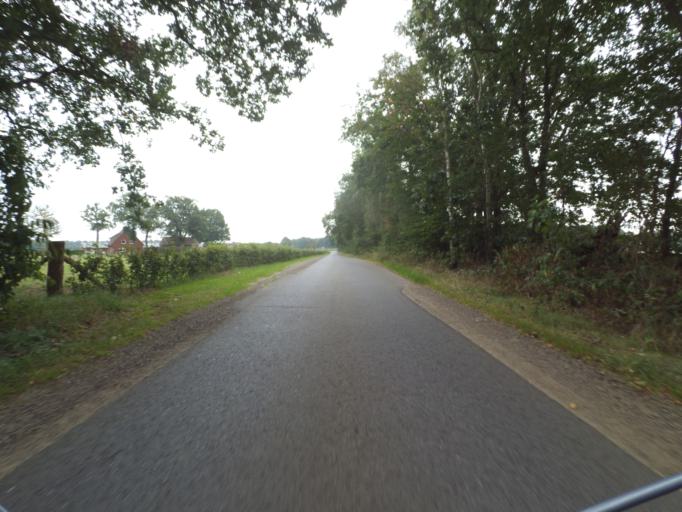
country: NL
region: Overijssel
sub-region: Gemeente Losser
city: Losser
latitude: 52.2760
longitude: 7.0536
